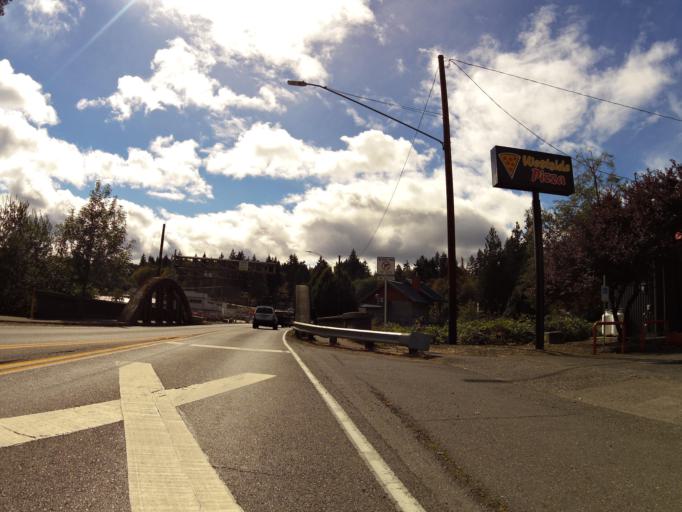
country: US
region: Washington
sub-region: Mason County
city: Shelton
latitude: 47.2096
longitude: -123.1008
